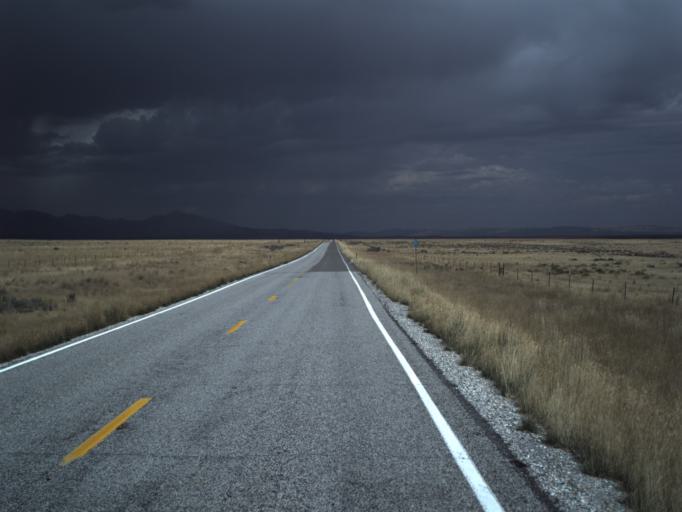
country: US
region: Idaho
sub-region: Minidoka County
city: Rupert
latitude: 41.8652
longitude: -113.1261
